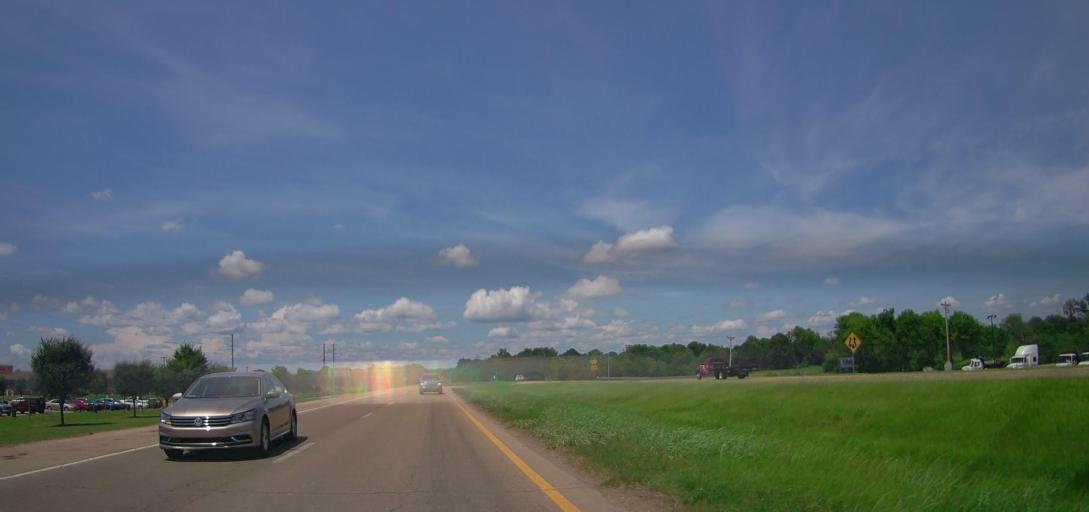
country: US
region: Mississippi
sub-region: Lee County
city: Tupelo
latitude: 34.3161
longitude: -88.7903
